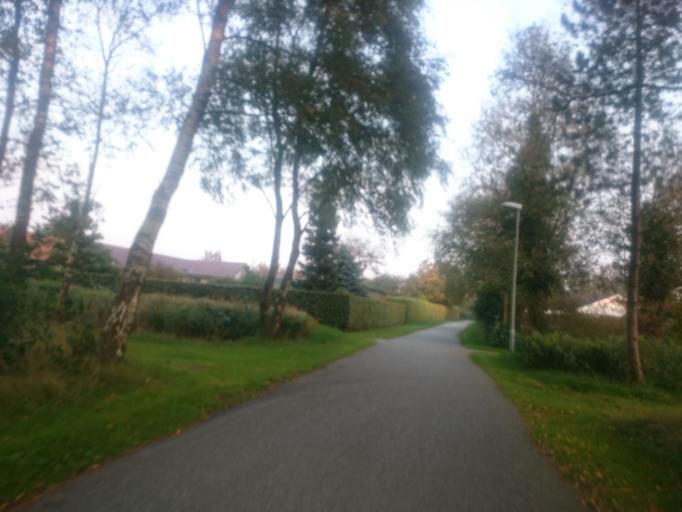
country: DK
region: South Denmark
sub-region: Billund Kommune
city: Billund
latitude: 55.7285
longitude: 9.1008
